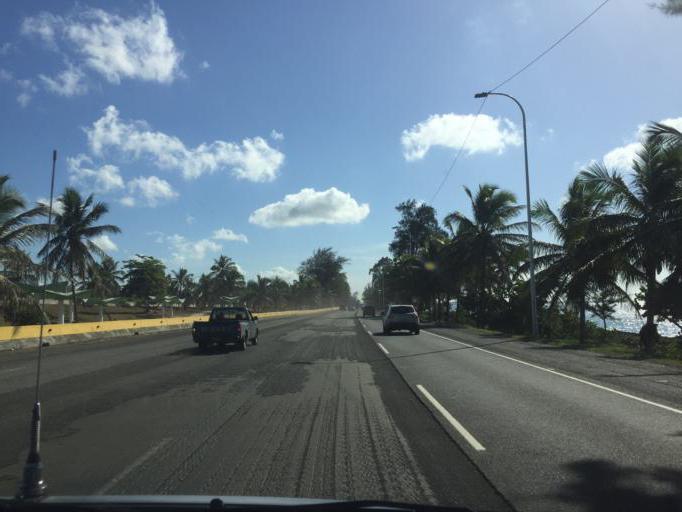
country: DO
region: Santo Domingo
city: Guerra
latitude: 18.4577
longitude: -69.7197
